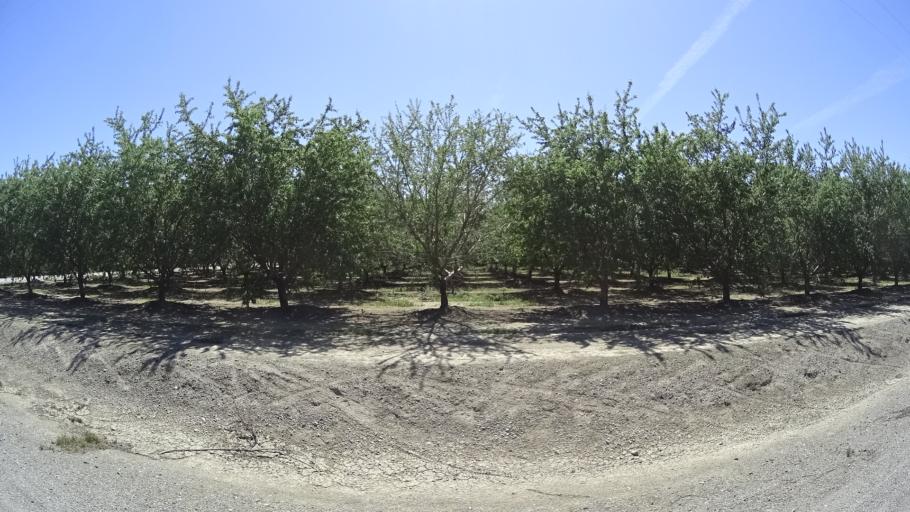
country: US
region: California
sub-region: Glenn County
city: Hamilton City
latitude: 39.7214
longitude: -122.0978
